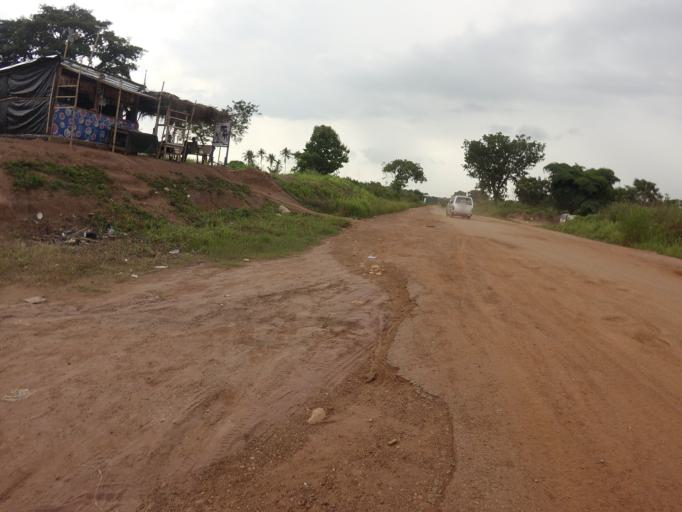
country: GH
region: Volta
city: Kpandu
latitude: 7.0038
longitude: 0.4334
